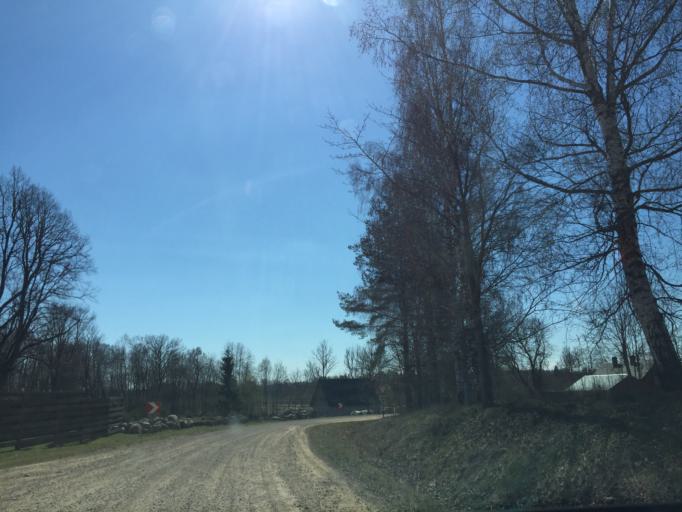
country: EE
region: Viljandimaa
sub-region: Viiratsi vald
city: Viiratsi
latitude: 58.3584
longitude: 25.7555
